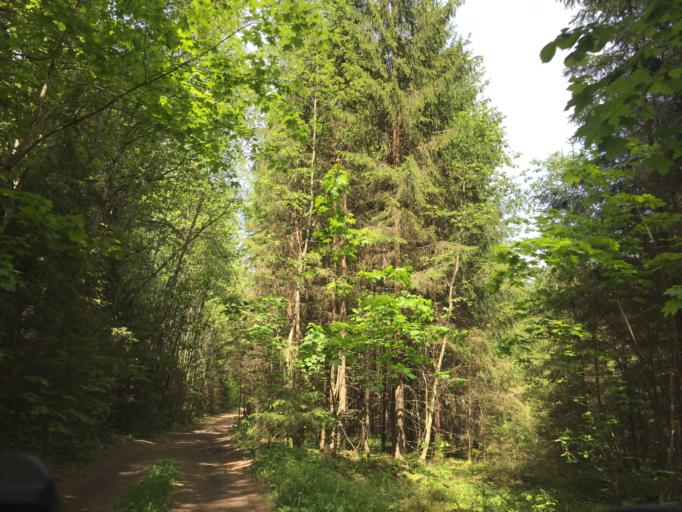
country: LV
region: Koceni
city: Koceni
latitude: 57.4403
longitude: 25.2840
